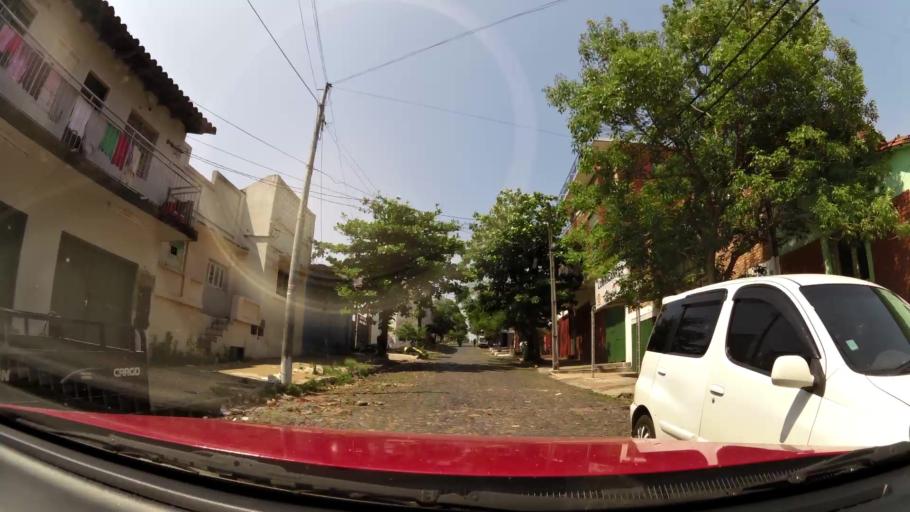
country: PY
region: Presidente Hayes
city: Nanawa
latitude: -25.2809
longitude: -57.6518
